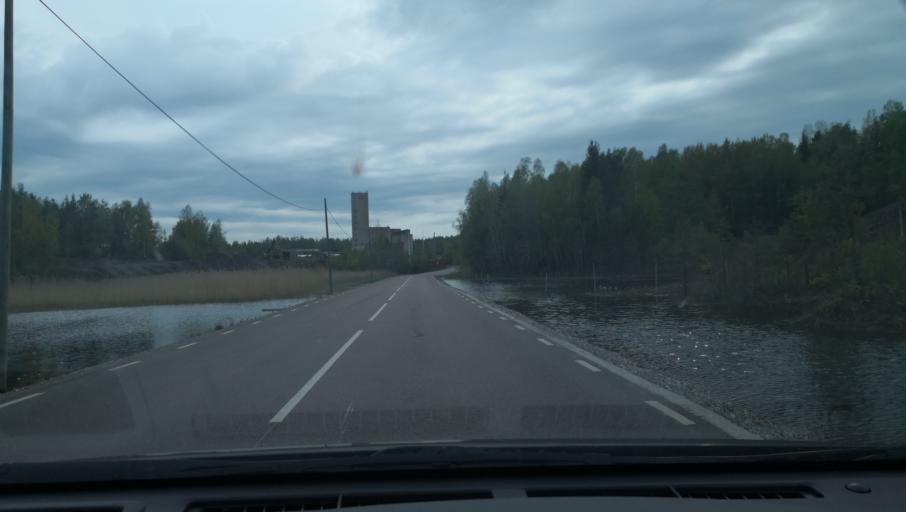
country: SE
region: Vaestmanland
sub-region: Skinnskattebergs Kommun
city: Skinnskatteberg
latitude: 59.8329
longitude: 15.5706
